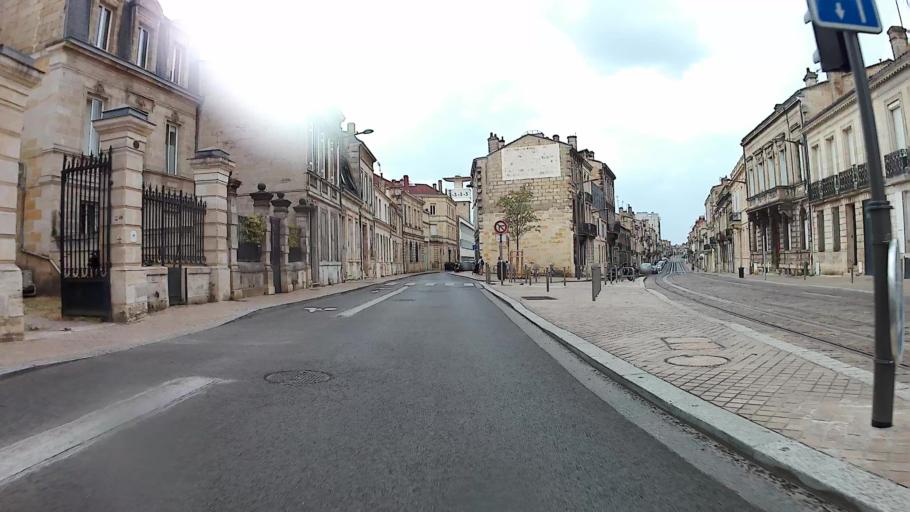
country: FR
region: Aquitaine
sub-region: Departement de la Gironde
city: Bordeaux
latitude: 44.8516
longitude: -0.5902
